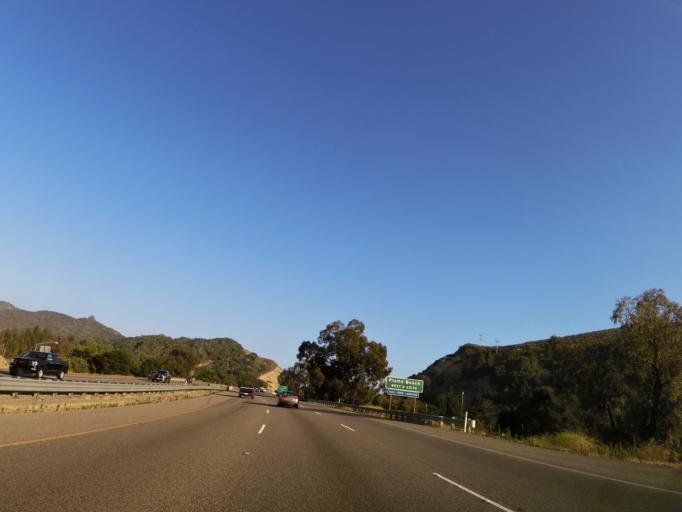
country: US
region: California
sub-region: San Luis Obispo County
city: Avila Beach
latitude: 35.1810
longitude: -120.7007
